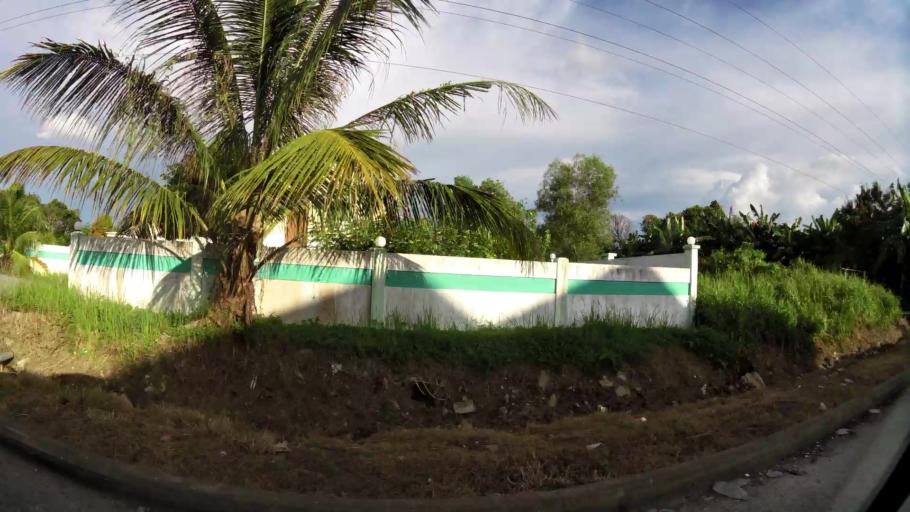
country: BN
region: Brunei and Muara
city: Bandar Seri Begawan
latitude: 4.9763
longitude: 114.9830
